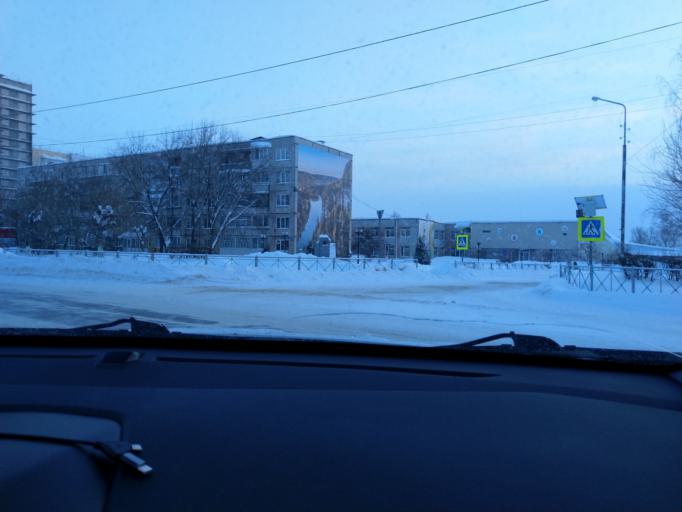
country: RU
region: Perm
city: Dobryanka
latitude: 58.4637
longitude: 56.3966
